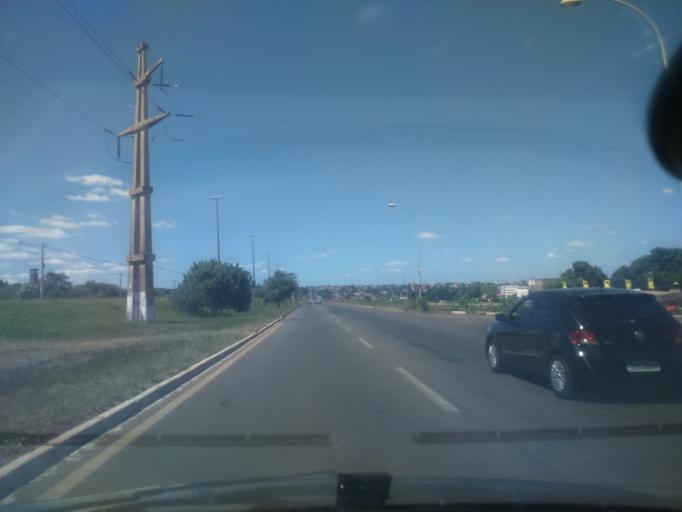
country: BR
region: Goias
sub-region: Luziania
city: Luziania
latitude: -16.0492
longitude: -48.0284
